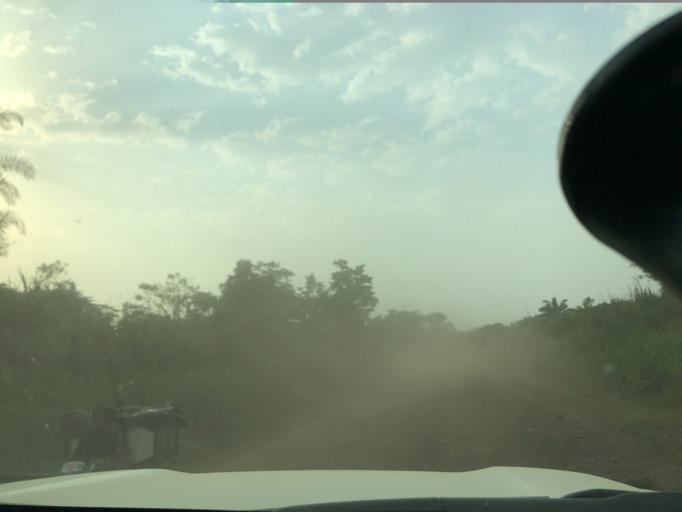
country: UG
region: Western Region
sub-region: Kasese District
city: Margherita
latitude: 0.2858
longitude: 29.6640
